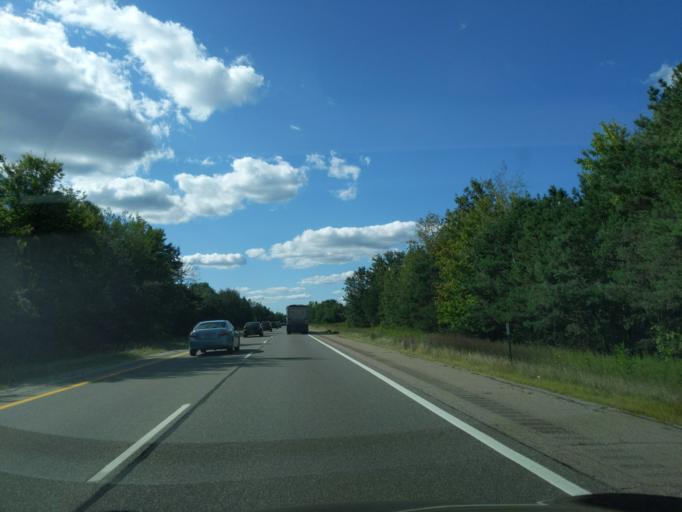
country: US
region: Michigan
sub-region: Muskegon County
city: Fruitport
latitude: 43.0984
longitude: -86.1056
